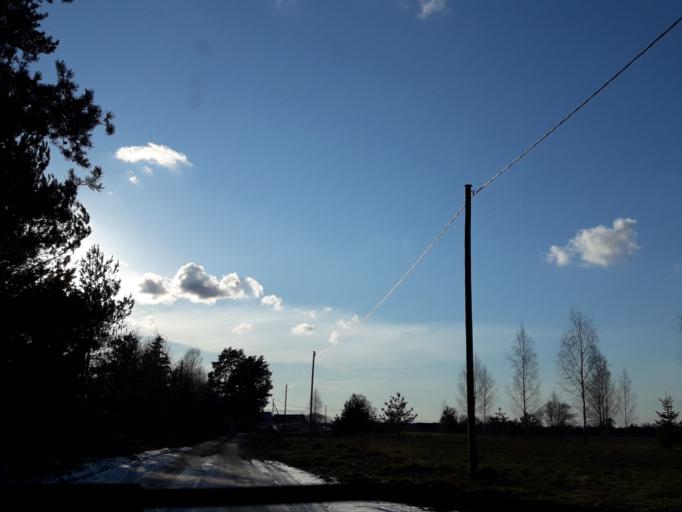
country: LV
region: Kekava
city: Kekava
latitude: 56.8743
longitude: 24.2082
